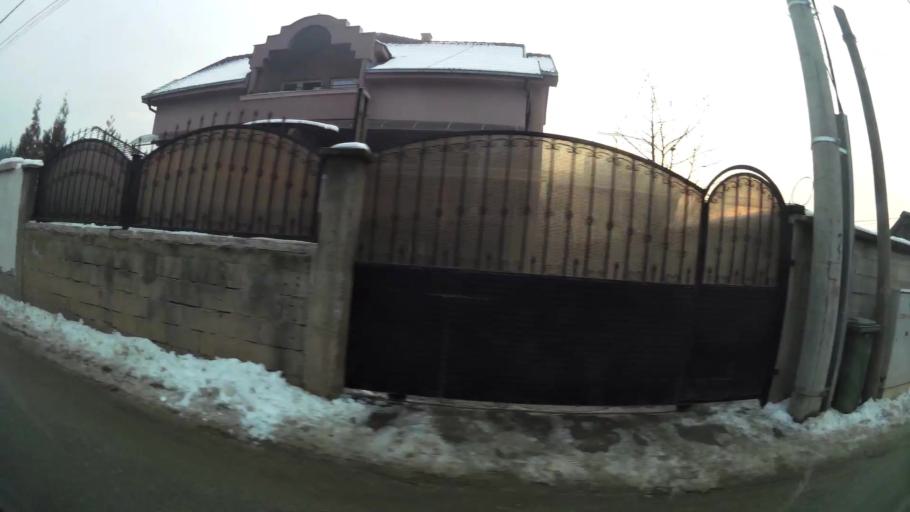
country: MK
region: Suto Orizari
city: Suto Orizare
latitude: 42.0355
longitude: 21.4137
